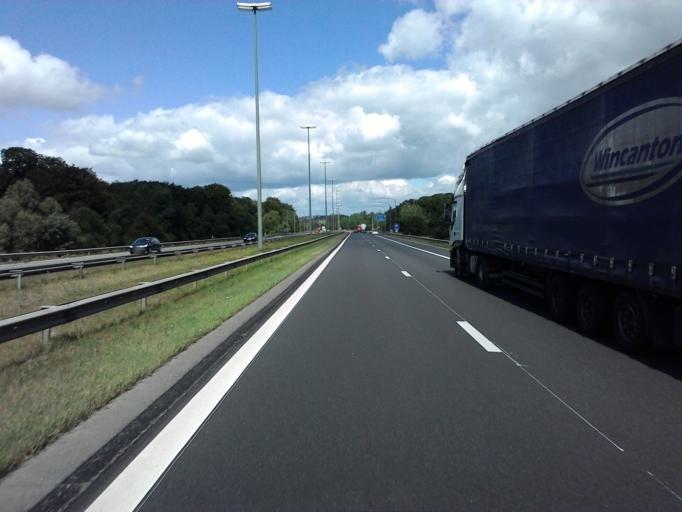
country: BE
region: Wallonia
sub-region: Province du Luxembourg
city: Arlon
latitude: 49.6821
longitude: 5.7561
